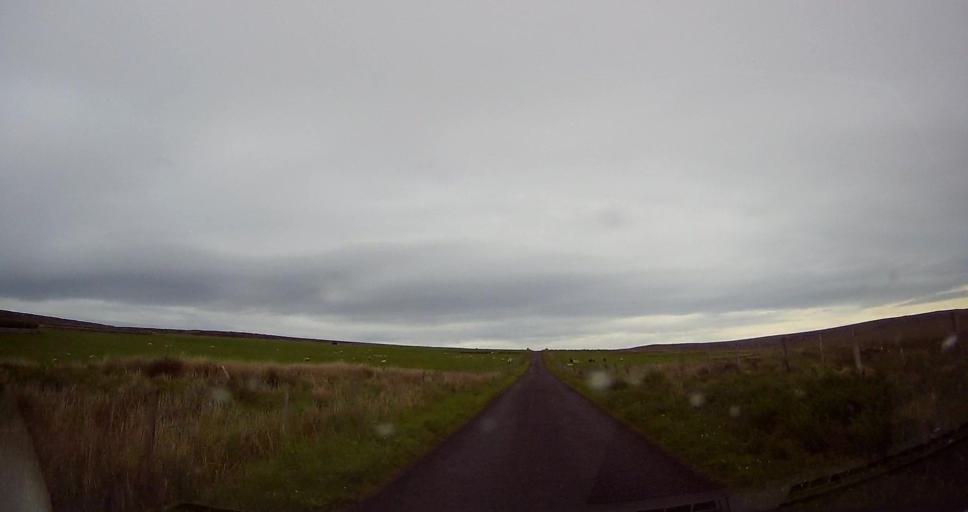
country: GB
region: Scotland
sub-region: Orkney Islands
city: Stromness
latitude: 59.0941
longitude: -3.1738
